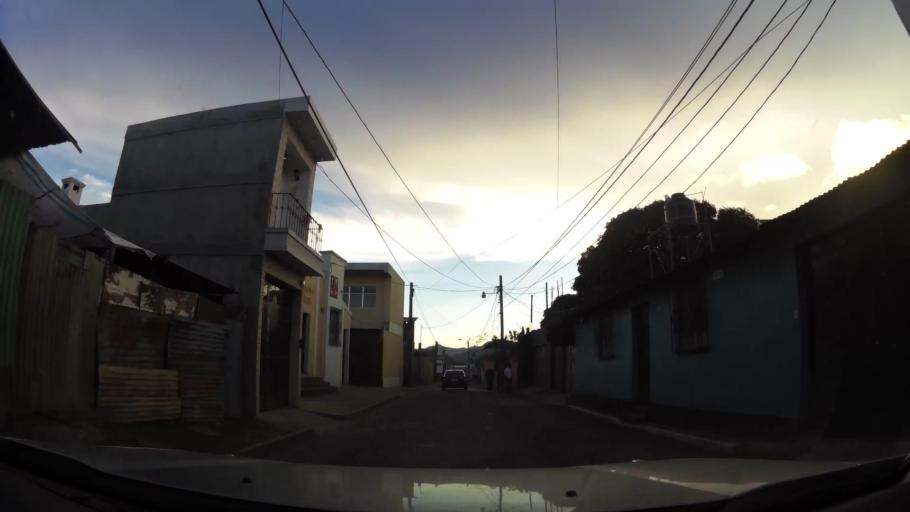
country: GT
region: Sacatepequez
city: San Lucas Sacatepequez
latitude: 14.6116
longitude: -90.6574
